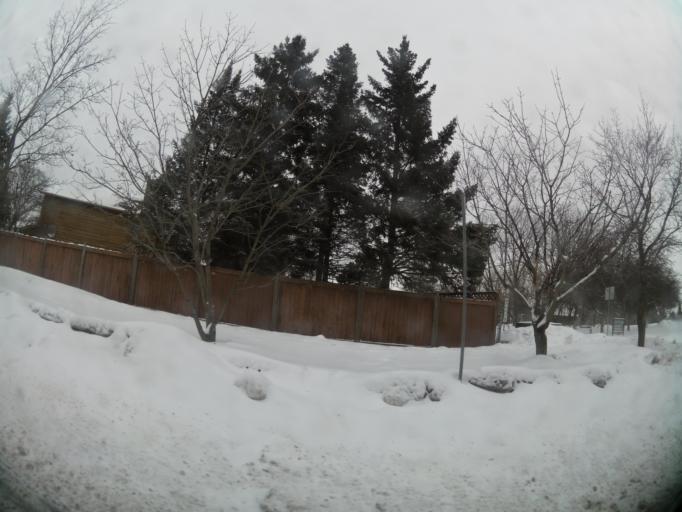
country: CA
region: Ontario
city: Ottawa
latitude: 45.3703
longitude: -75.6205
